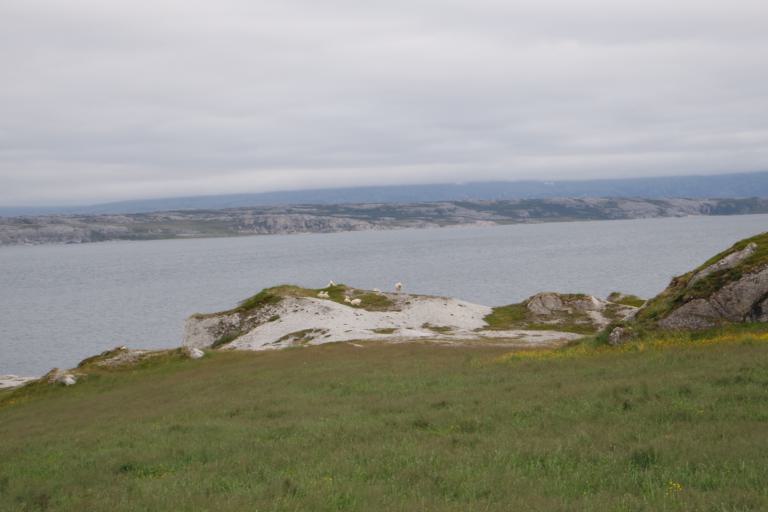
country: NO
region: Finnmark Fylke
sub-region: Porsanger
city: Lakselv
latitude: 70.3015
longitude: 25.1730
